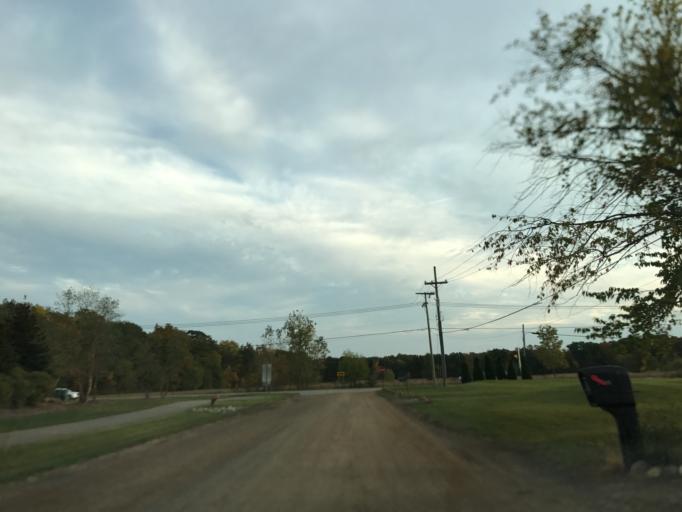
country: US
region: Michigan
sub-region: Oakland County
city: South Lyon
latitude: 42.4773
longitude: -83.6182
